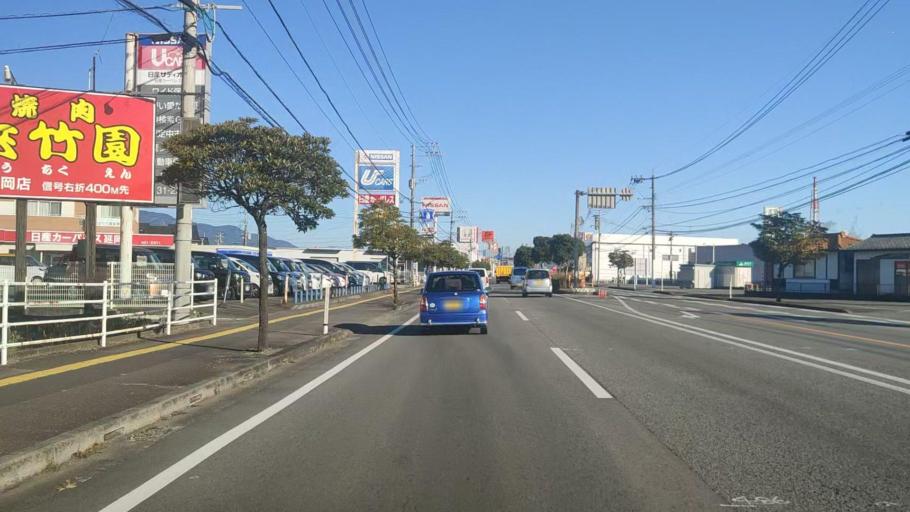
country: JP
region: Miyazaki
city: Nobeoka
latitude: 32.5589
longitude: 131.6803
